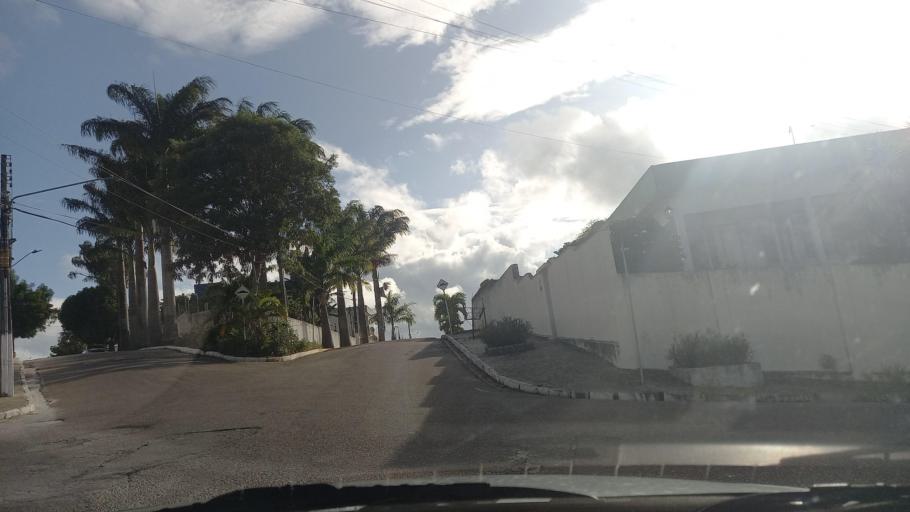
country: BR
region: Pernambuco
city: Garanhuns
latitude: -8.8945
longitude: -36.4976
